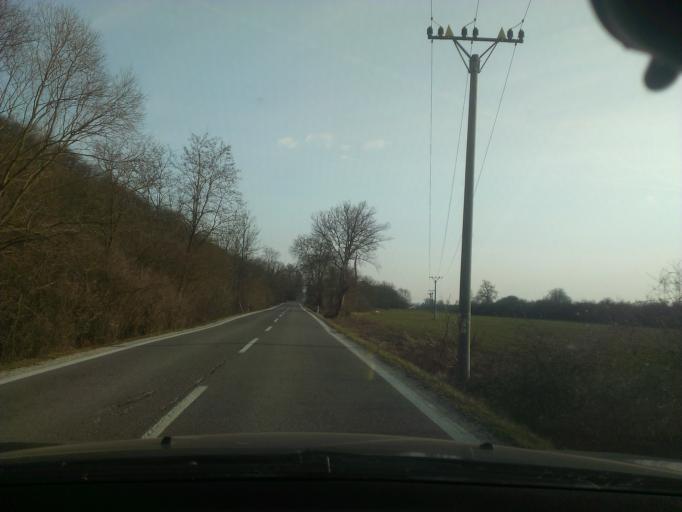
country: SK
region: Trenciansky
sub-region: Okres Nove Mesto nad Vahom
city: Nove Mesto nad Vahom
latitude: 48.6789
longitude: 17.8757
